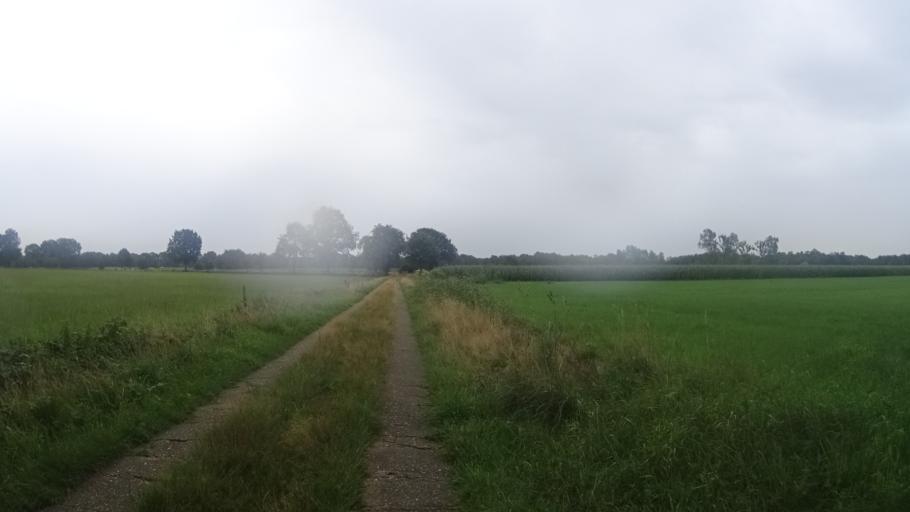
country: DE
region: Schleswig-Holstein
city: Heede
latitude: 53.7604
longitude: 9.7961
